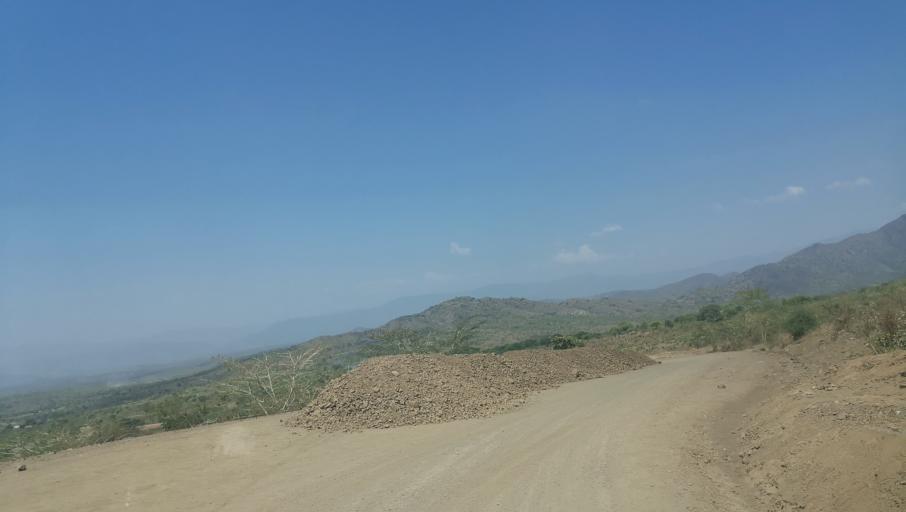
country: ET
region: Southern Nations, Nationalities, and People's Region
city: Arba Minch'
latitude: 6.3342
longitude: 37.3293
